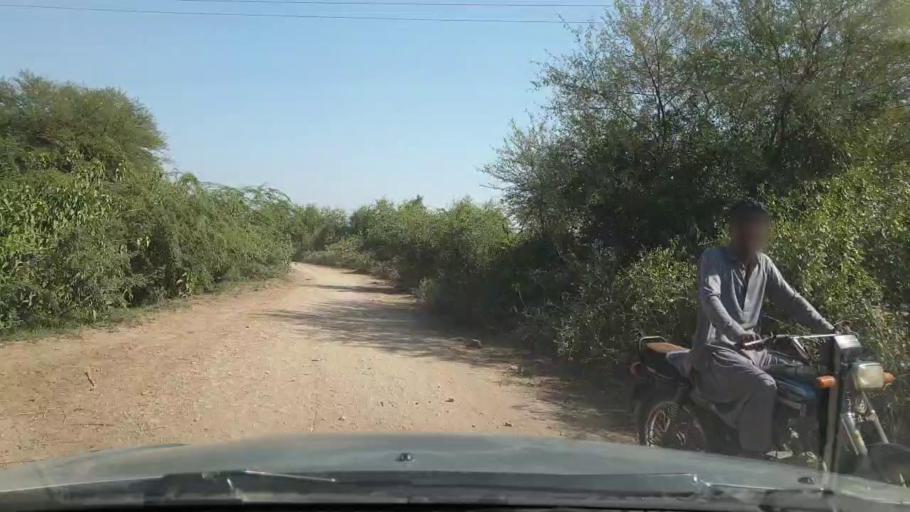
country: PK
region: Sindh
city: Kario
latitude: 24.9454
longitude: 68.5352
